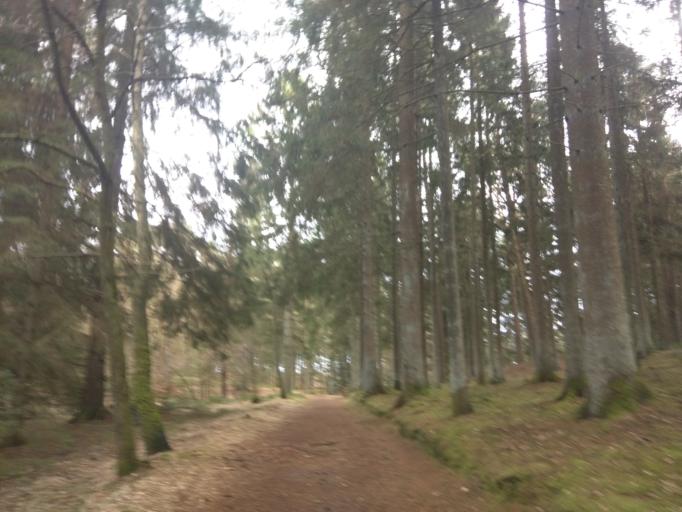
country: DK
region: Central Jutland
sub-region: Silkeborg Kommune
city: Silkeborg
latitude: 56.1797
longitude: 9.5255
